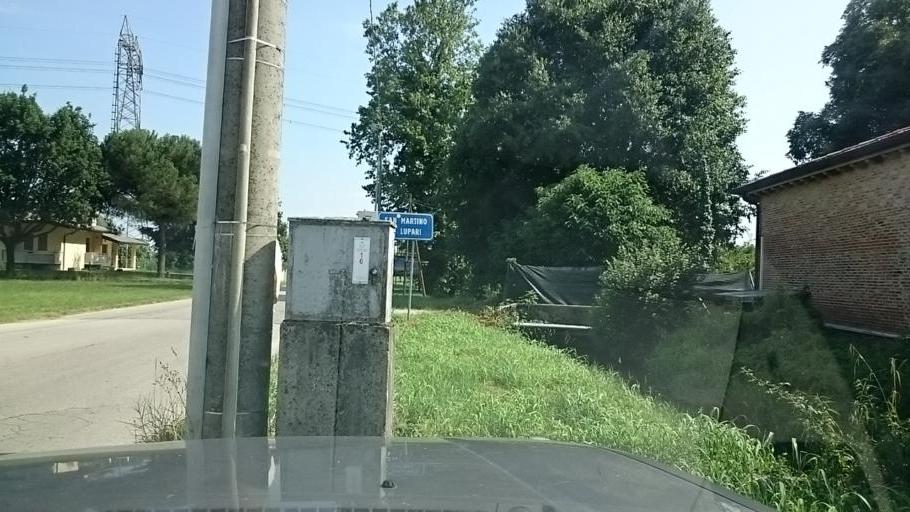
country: IT
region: Veneto
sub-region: Provincia di Padova
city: Galliera Veneta
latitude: 45.6856
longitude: 11.8247
